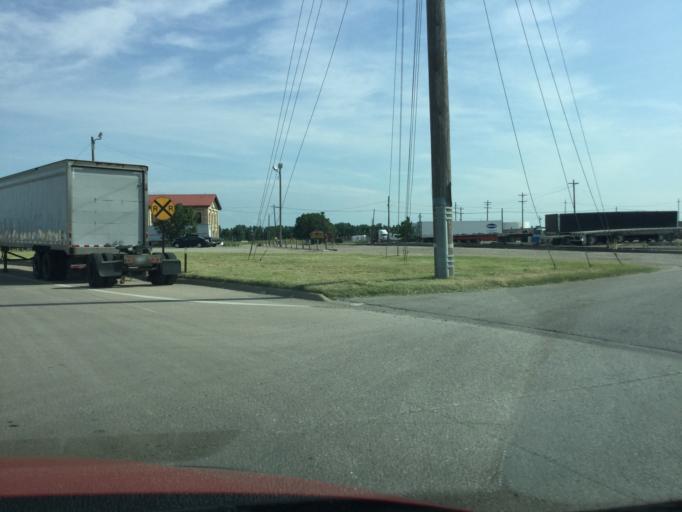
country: US
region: Kansas
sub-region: Shawnee County
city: Topeka
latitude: 39.0570
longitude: -95.6633
